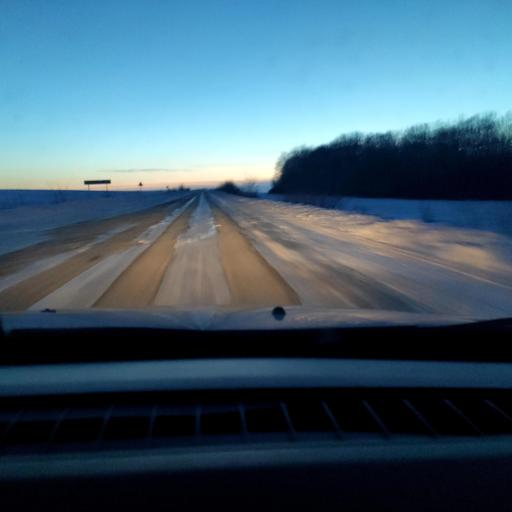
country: RU
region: Samara
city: Georgiyevka
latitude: 53.3140
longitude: 50.8440
